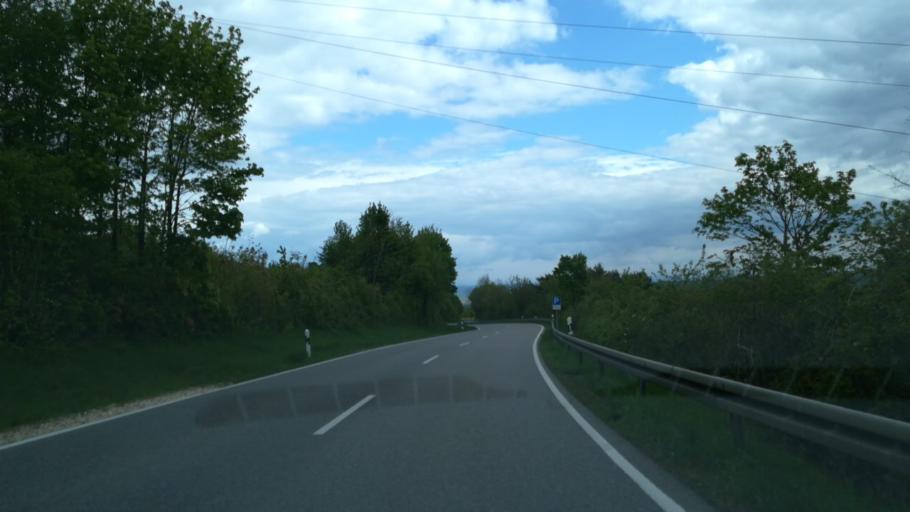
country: DE
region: Baden-Wuerttemberg
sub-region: Freiburg Region
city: Tengen
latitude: 47.8229
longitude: 8.6394
